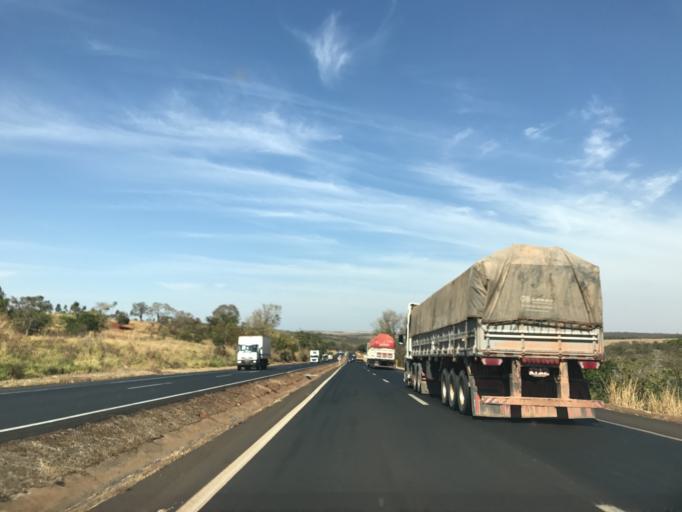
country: BR
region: Minas Gerais
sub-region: Monte Alegre De Minas
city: Monte Alegre de Minas
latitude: -18.7792
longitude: -49.0778
